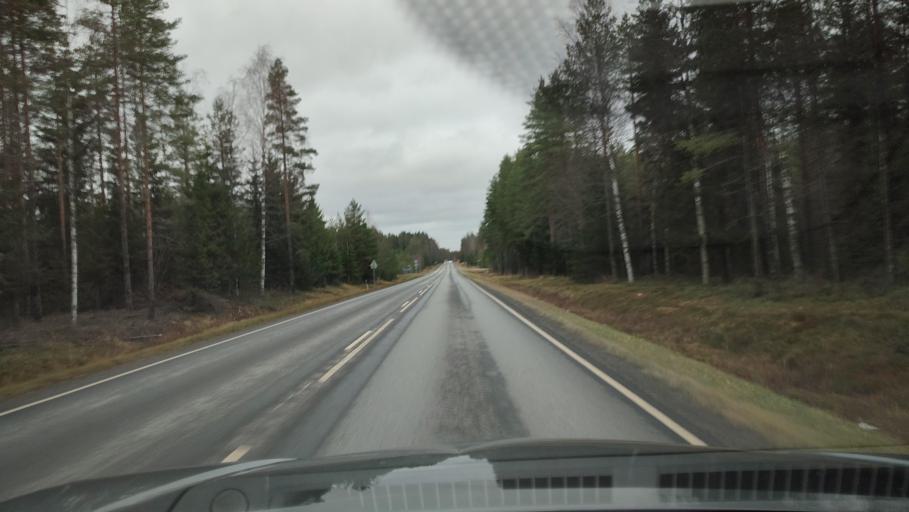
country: FI
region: Southern Ostrobothnia
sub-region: Seinaejoki
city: Kurikka
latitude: 62.5366
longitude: 22.3336
